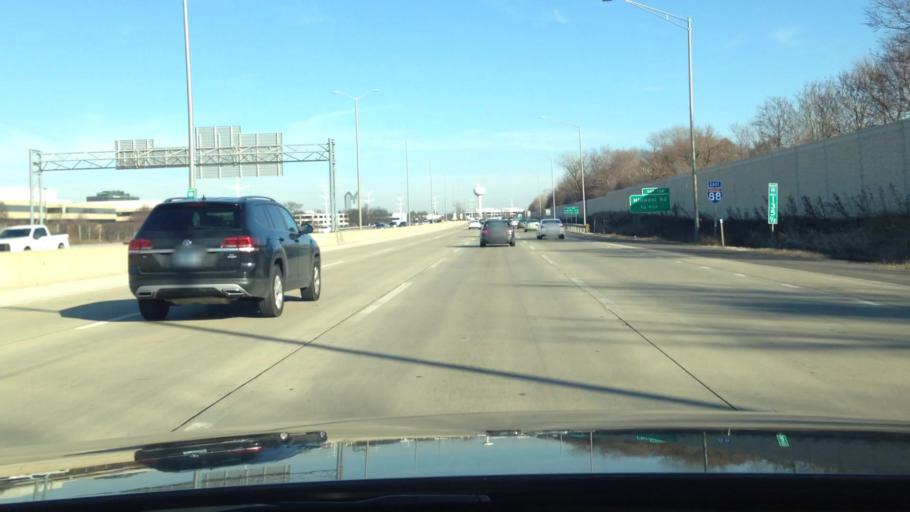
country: US
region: Illinois
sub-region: DuPage County
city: Oakbrook Terrace
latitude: 41.8401
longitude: -87.9897
